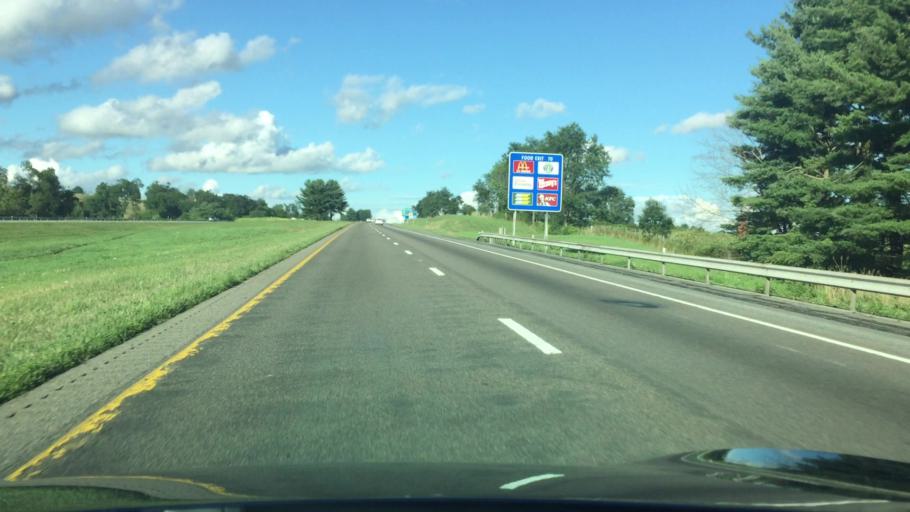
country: US
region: Virginia
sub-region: Wythe County
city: Wytheville
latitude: 36.9527
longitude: -81.1220
